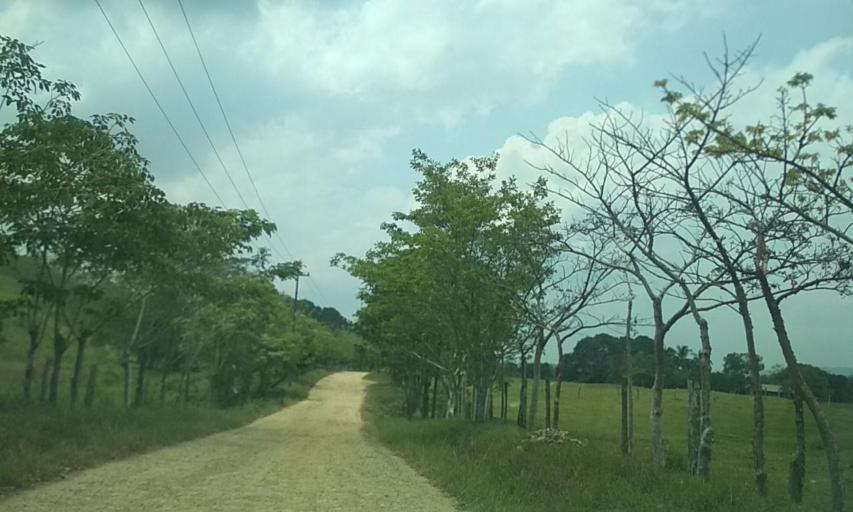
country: MX
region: Tabasco
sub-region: Huimanguillo
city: Francisco Rueda
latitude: 17.5861
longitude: -93.7907
